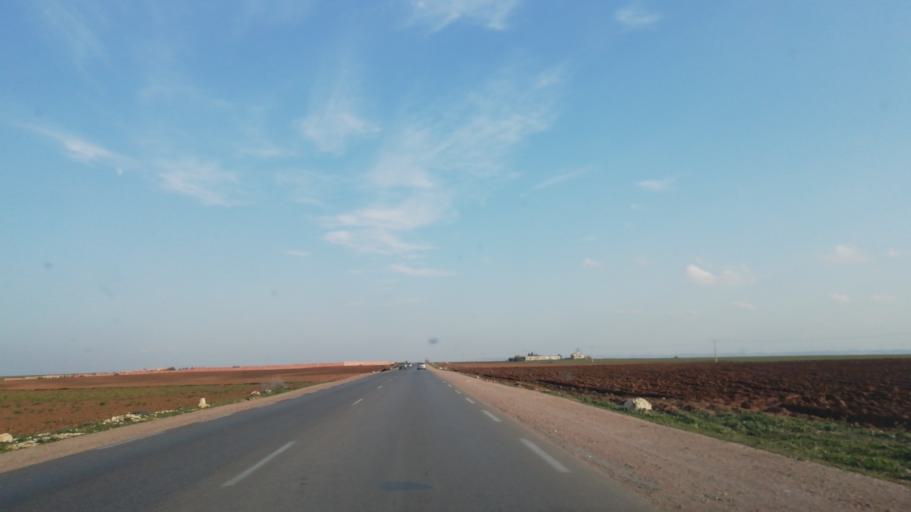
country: DZ
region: Relizane
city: Relizane
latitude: 35.8939
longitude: 0.6090
